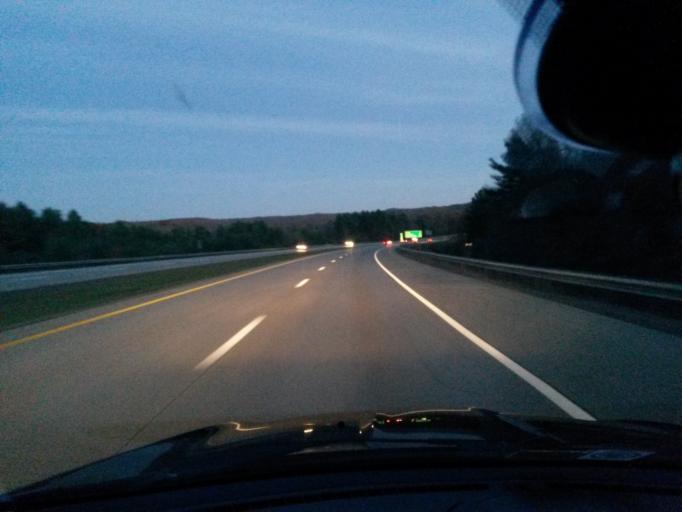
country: US
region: West Virginia
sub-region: Raleigh County
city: Daniels
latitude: 37.7730
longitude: -81.0521
